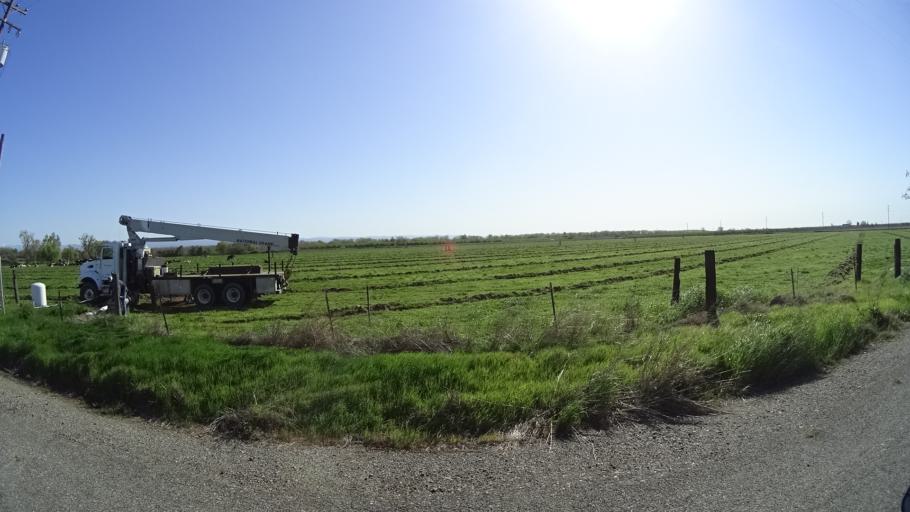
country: US
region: California
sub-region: Glenn County
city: Hamilton City
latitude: 39.7784
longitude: -122.0477
